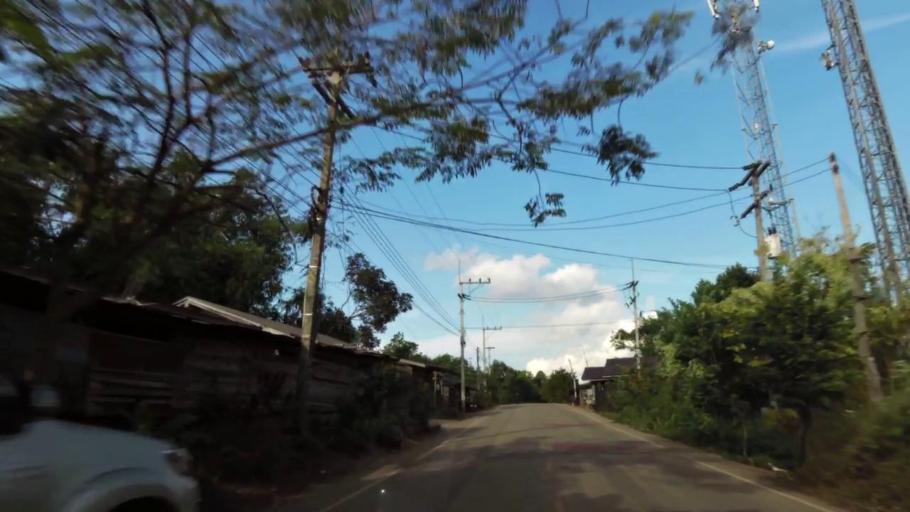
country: TH
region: Chiang Rai
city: Khun Tan
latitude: 19.8698
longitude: 100.3398
